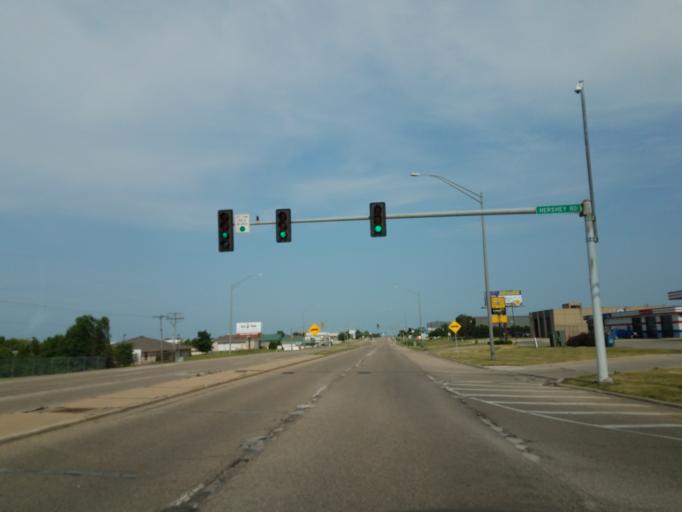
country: US
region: Illinois
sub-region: McLean County
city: Bloomington
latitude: 40.4883
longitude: -88.9430
